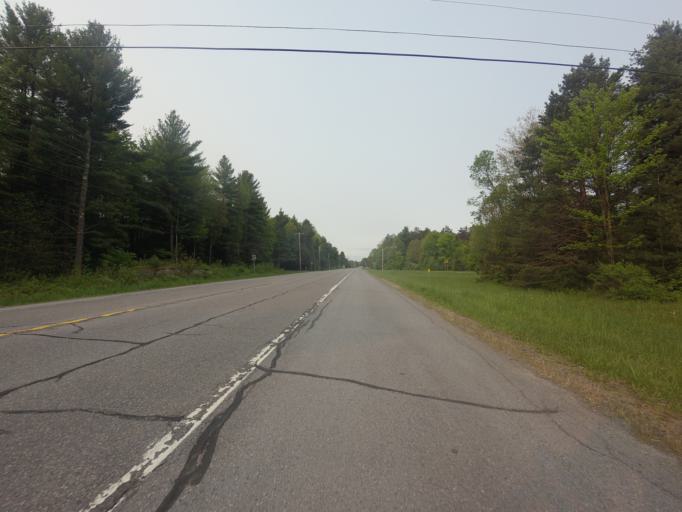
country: US
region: New York
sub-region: Jefferson County
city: Carthage
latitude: 44.0871
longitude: -75.4296
